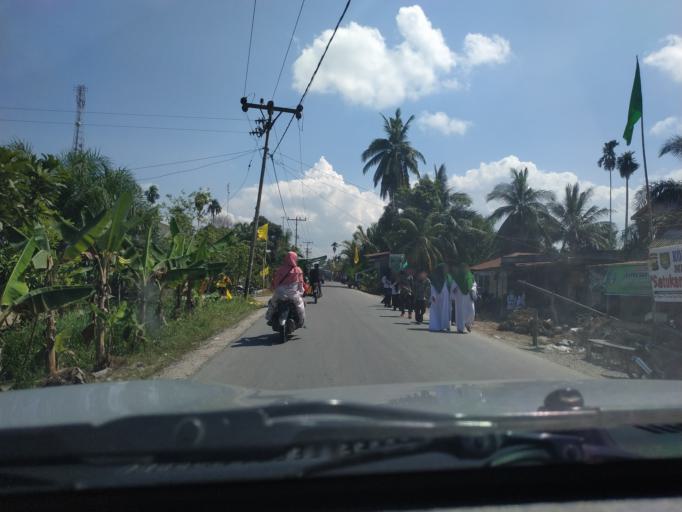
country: ID
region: North Sumatra
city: Tanjungbalai
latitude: 2.9311
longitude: 99.8601
